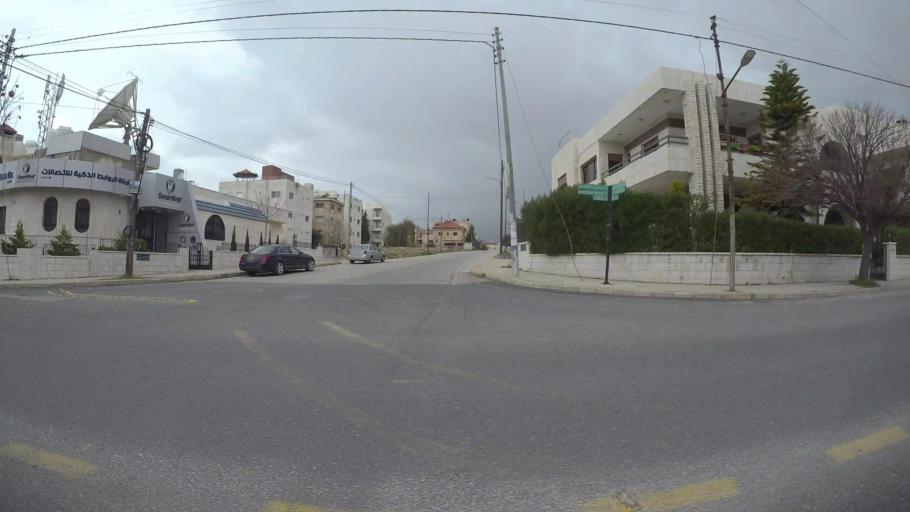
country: JO
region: Amman
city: Wadi as Sir
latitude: 31.9697
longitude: 35.8524
